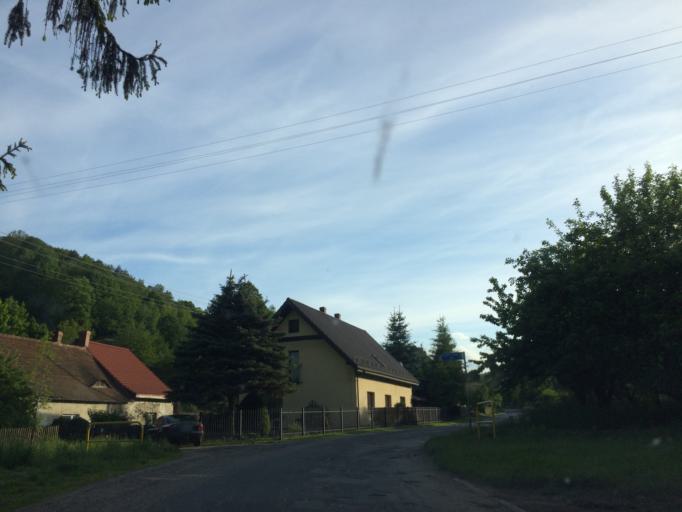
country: PL
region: Lower Silesian Voivodeship
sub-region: Powiat walbrzyski
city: Walim
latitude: 50.7492
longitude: 16.5023
